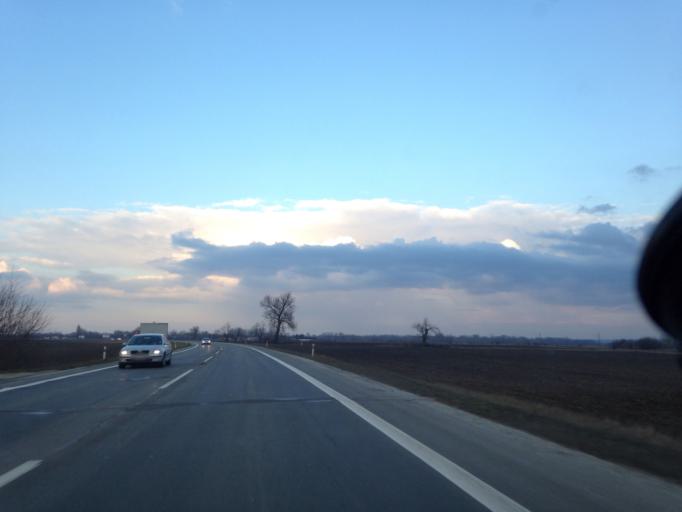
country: SK
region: Nitriansky
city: Komarno
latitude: 47.7986
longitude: 18.1832
